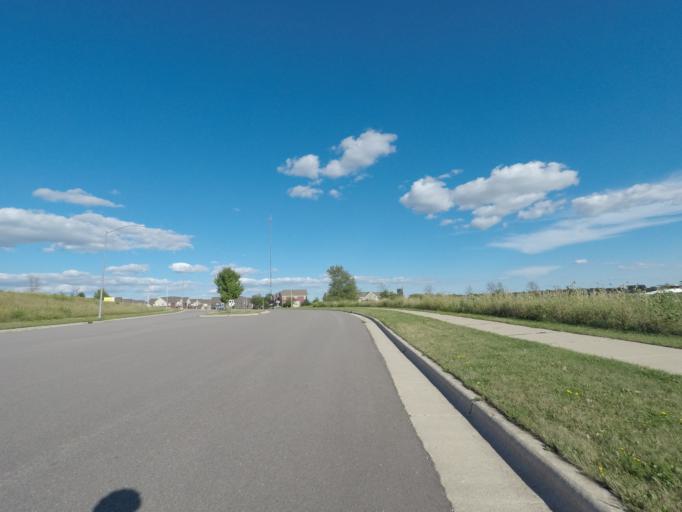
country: US
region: Wisconsin
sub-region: Dane County
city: Middleton
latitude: 43.0578
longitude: -89.5539
